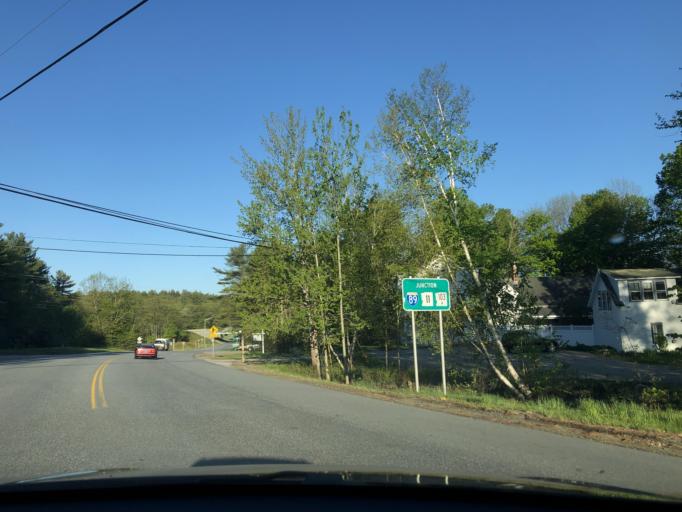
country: US
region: New Hampshire
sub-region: Merrimack County
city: New London
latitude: 43.4233
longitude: -72.0335
